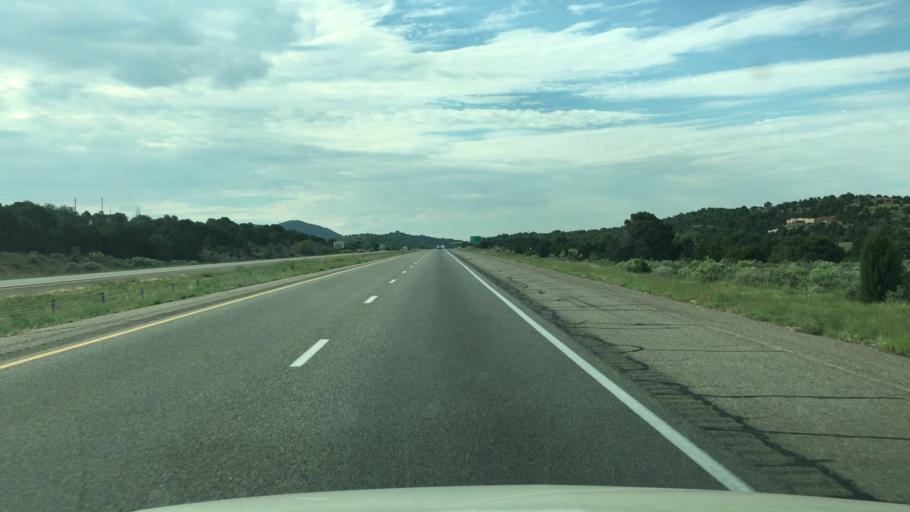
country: US
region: New Mexico
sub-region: Santa Fe County
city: Santa Fe
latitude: 35.6317
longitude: -105.9252
